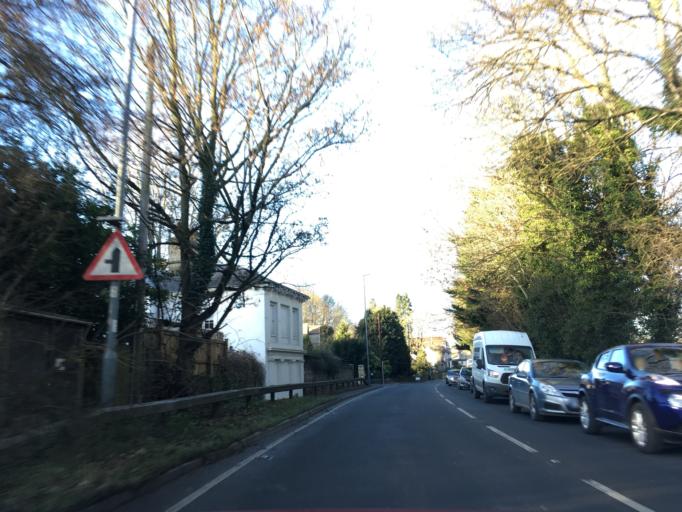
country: GB
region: England
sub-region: Bath and North East Somerset
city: Saltford
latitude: 51.3962
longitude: -2.4485
